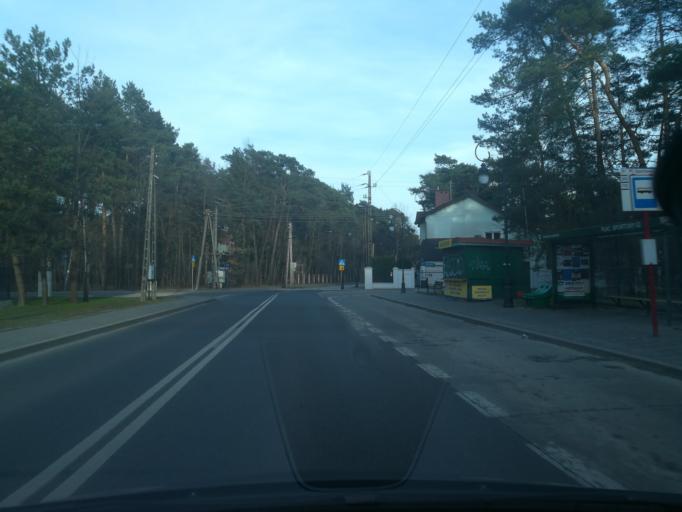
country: PL
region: Masovian Voivodeship
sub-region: Powiat piaseczynski
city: Konstancin-Jeziorna
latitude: 52.0779
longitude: 21.1109
